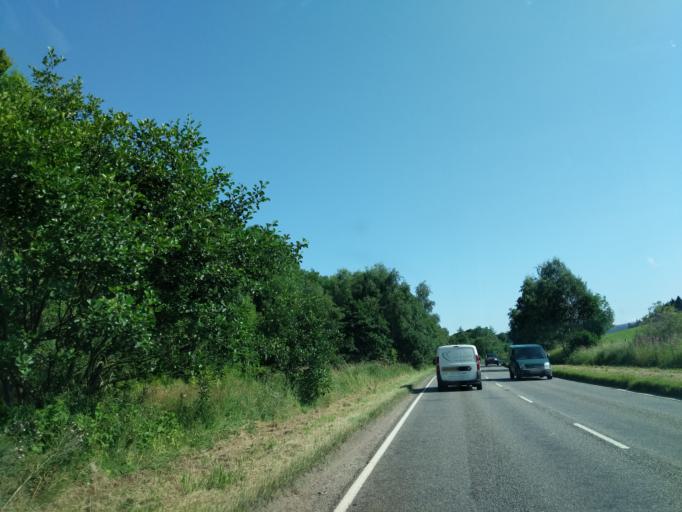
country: GB
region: Scotland
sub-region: Moray
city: Rothes
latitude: 57.5045
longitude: -3.1950
